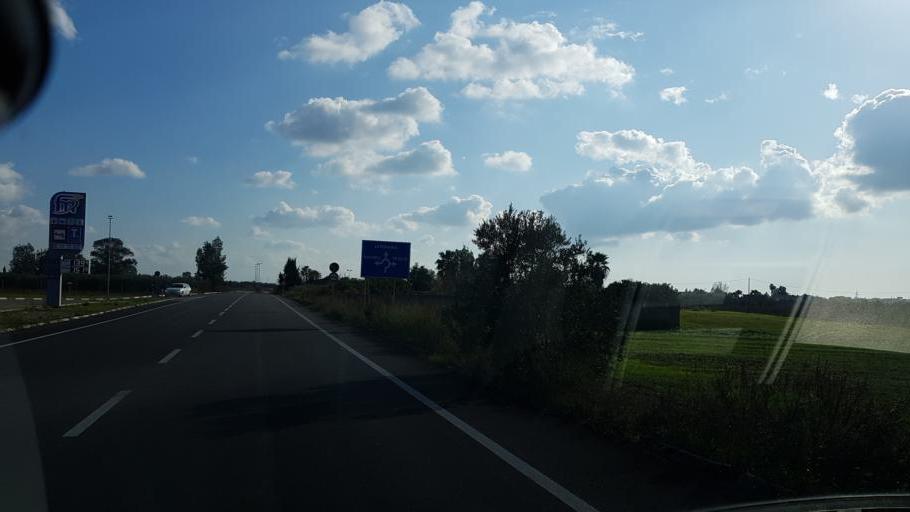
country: IT
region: Apulia
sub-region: Provincia di Lecce
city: Veglie
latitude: 40.3414
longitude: 17.9784
